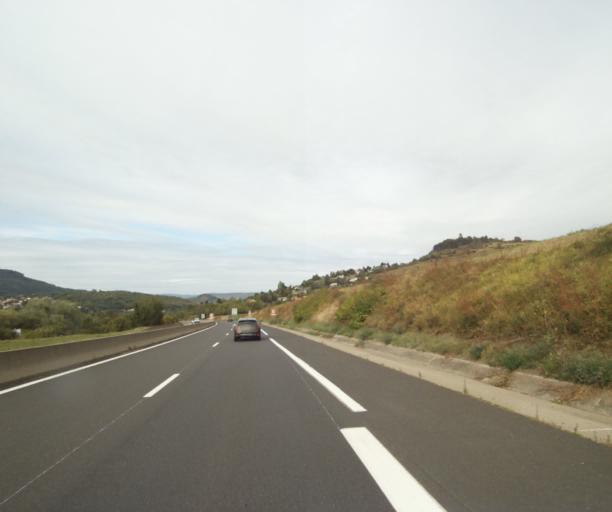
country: FR
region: Auvergne
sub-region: Departement du Puy-de-Dome
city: Ceyrat
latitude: 45.7234
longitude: 3.0719
